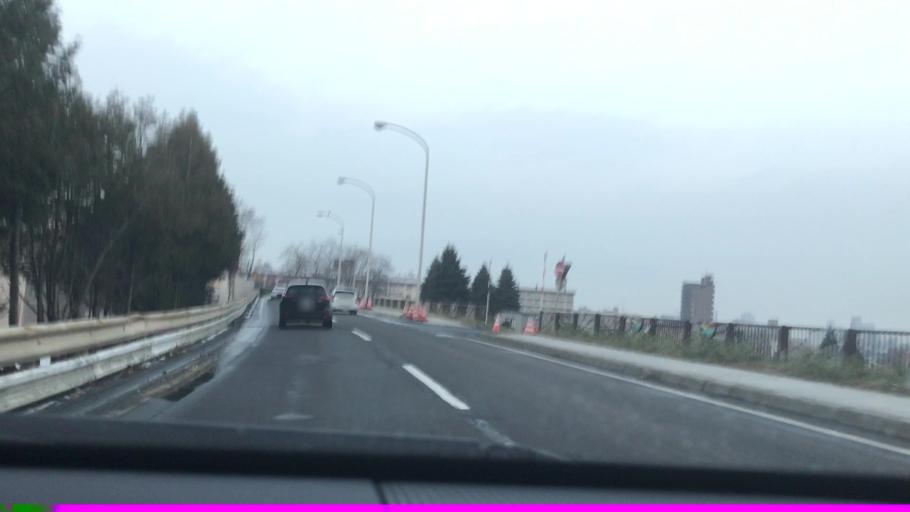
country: JP
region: Hokkaido
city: Sapporo
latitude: 43.0202
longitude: 141.3513
